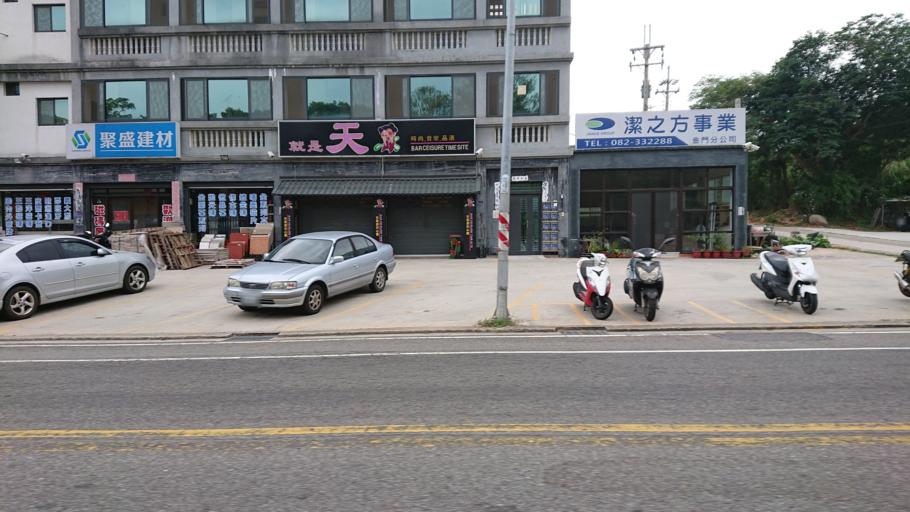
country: TW
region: Fukien
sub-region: Kinmen
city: Jincheng
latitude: 24.4420
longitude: 118.3902
